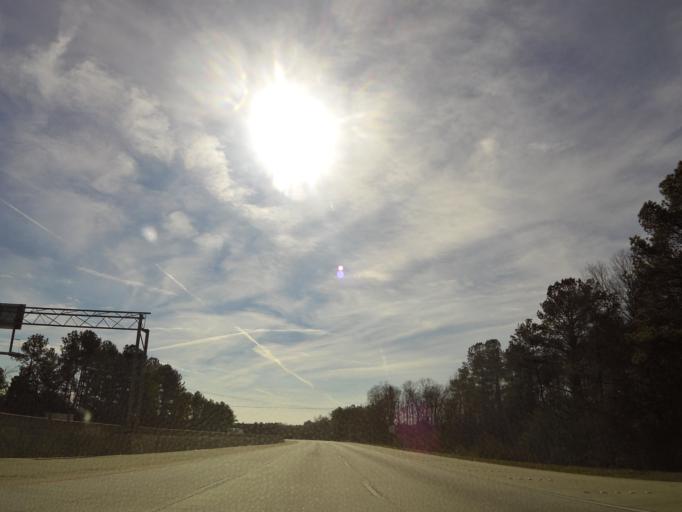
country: US
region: Georgia
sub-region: Coweta County
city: East Newnan
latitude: 33.3160
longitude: -84.7850
